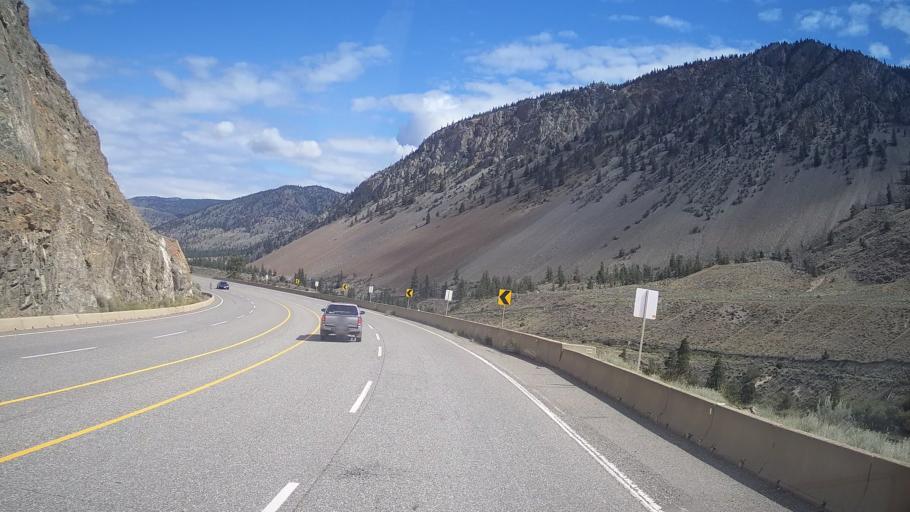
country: CA
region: British Columbia
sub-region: Thompson-Nicola Regional District
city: Ashcroft
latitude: 50.5113
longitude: -121.2816
